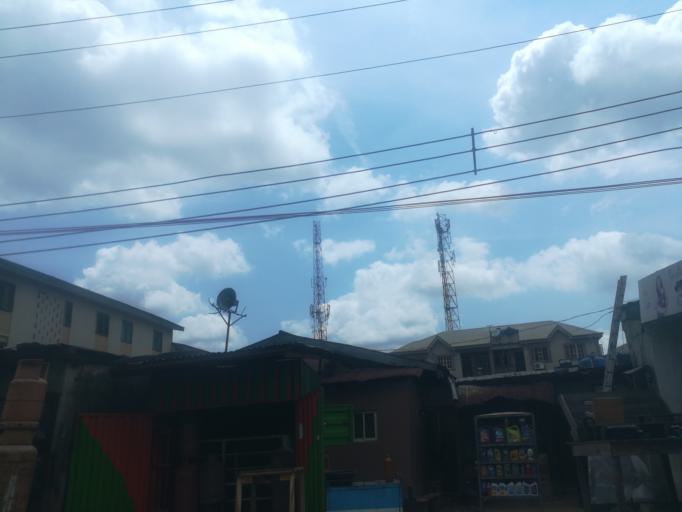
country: NG
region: Lagos
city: Somolu
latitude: 6.5563
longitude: 3.3871
